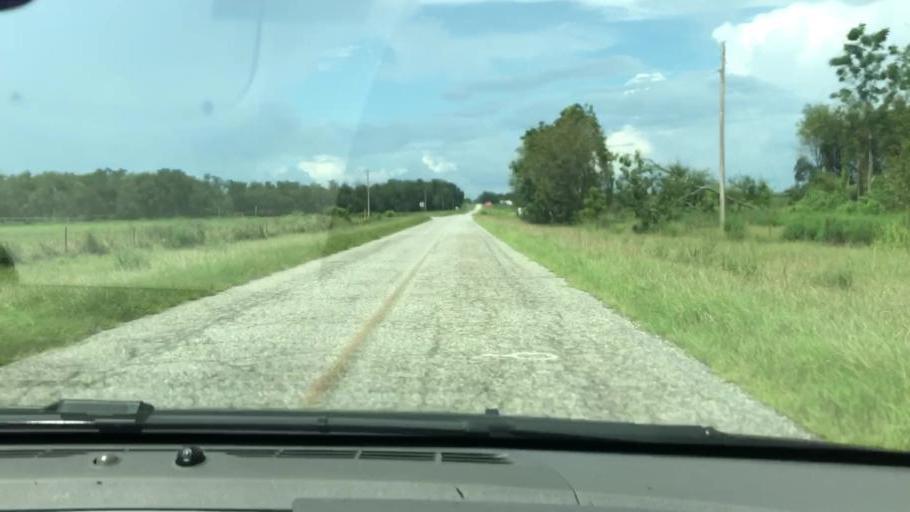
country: US
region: Georgia
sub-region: Seminole County
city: Donalsonville
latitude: 31.1798
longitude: -85.0045
